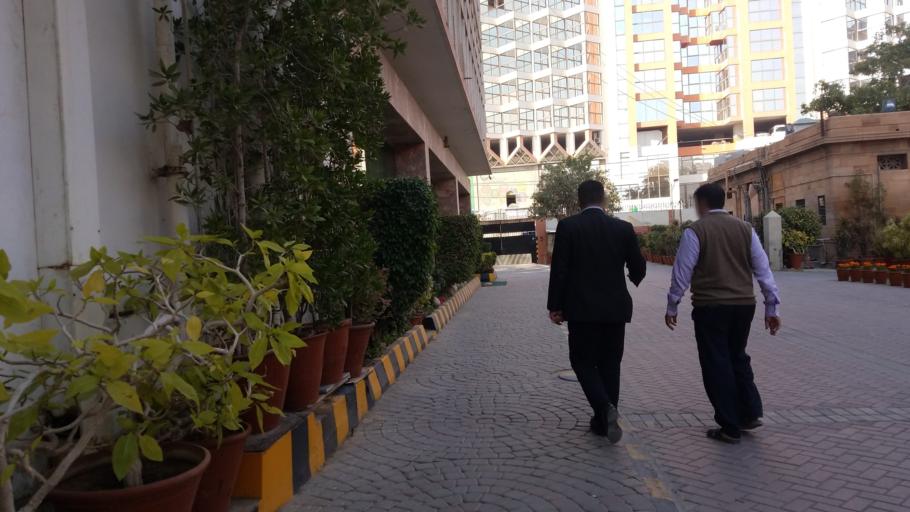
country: PK
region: Sindh
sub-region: Karachi District
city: Karachi
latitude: 24.8486
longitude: 66.9989
